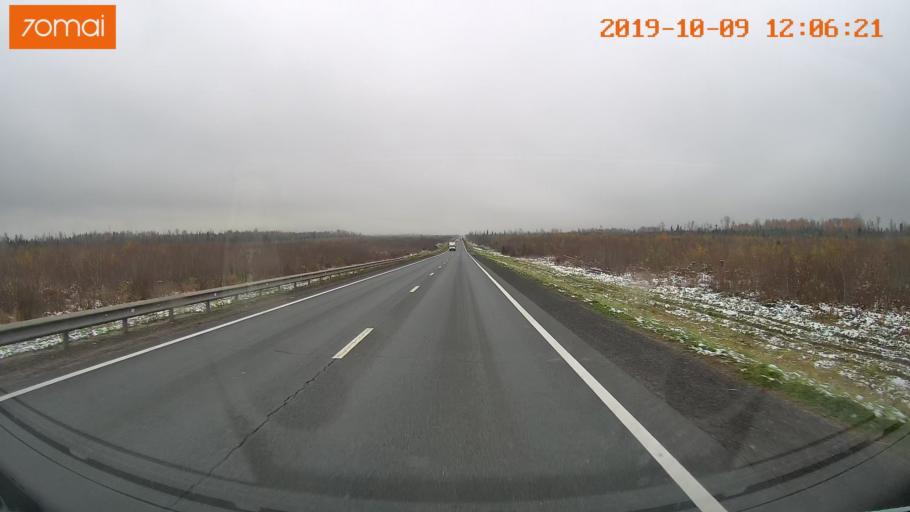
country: RU
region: Jaroslavl
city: Prechistoye
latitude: 58.6156
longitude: 40.3347
